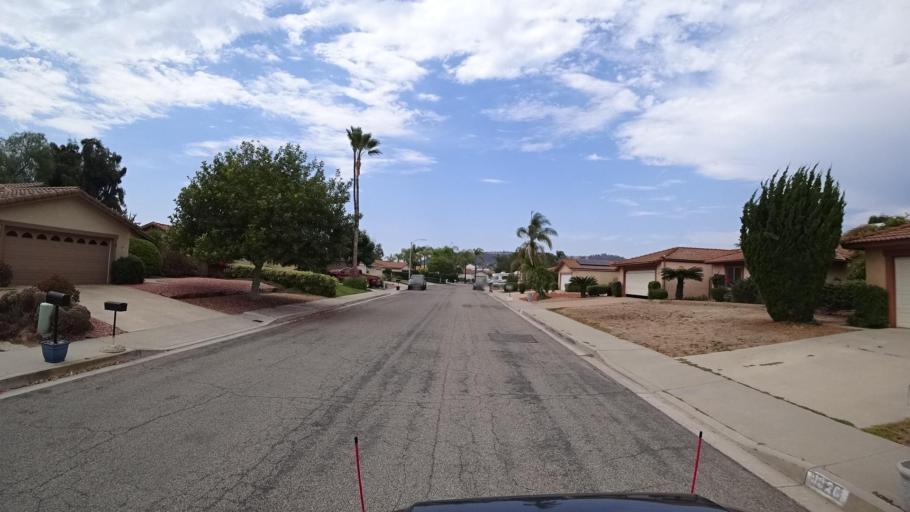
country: US
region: California
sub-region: San Diego County
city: Escondido
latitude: 33.1522
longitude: -117.1159
